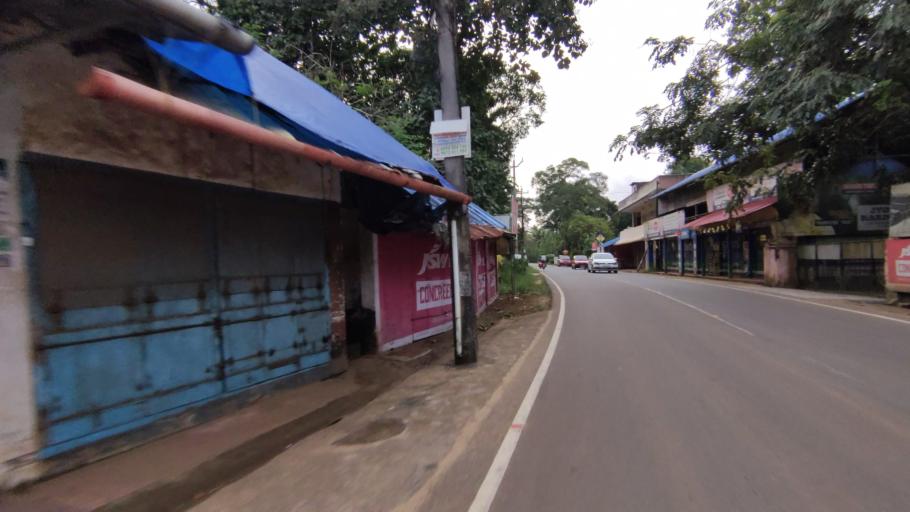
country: IN
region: Kerala
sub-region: Alappuzha
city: Shertallai
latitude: 9.6578
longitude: 76.3662
